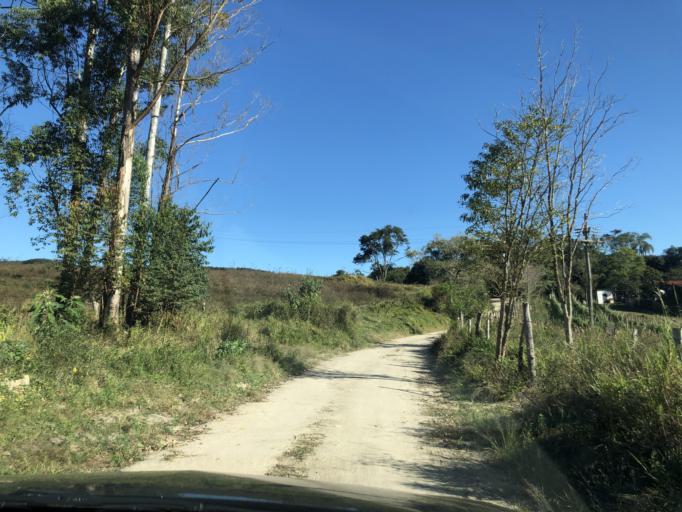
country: BR
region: Sao Paulo
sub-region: Pilar Do Sul
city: Pilar do Sul
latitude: -23.8247
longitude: -47.6277
